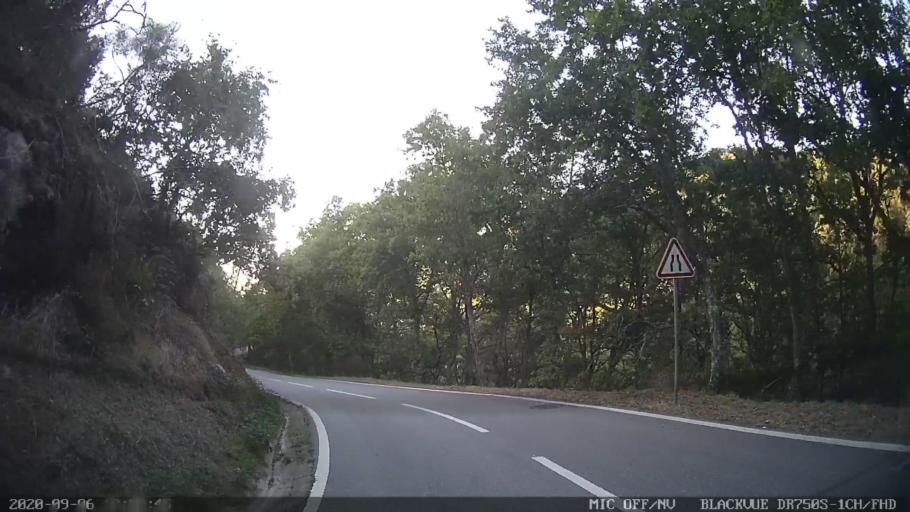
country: PT
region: Porto
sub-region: Baiao
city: Baiao
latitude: 41.2219
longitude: -7.9910
